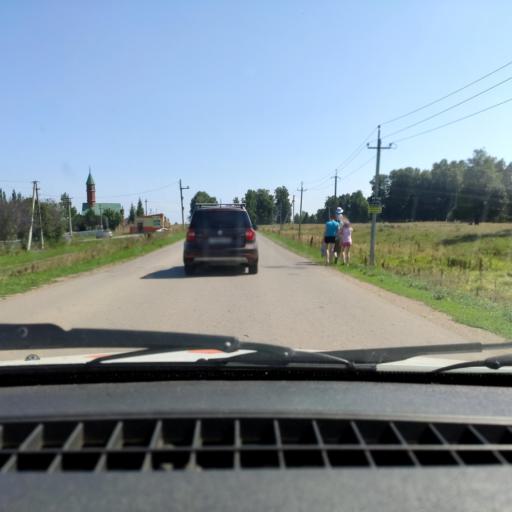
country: RU
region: Bashkortostan
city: Kudeyevskiy
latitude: 54.8832
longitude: 56.6292
